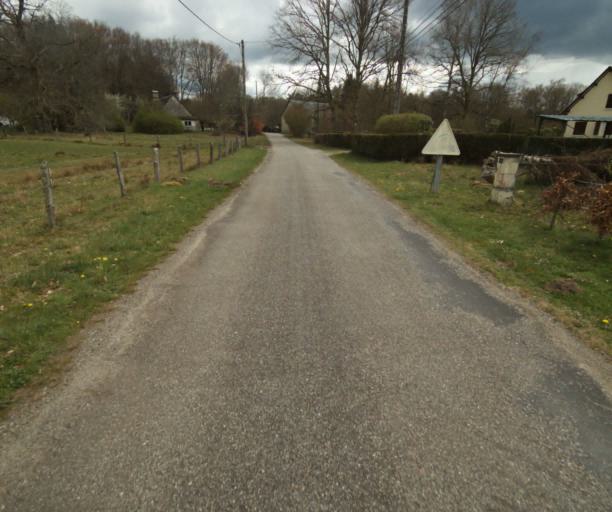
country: FR
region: Limousin
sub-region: Departement de la Correze
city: Correze
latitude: 45.2749
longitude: 1.9803
